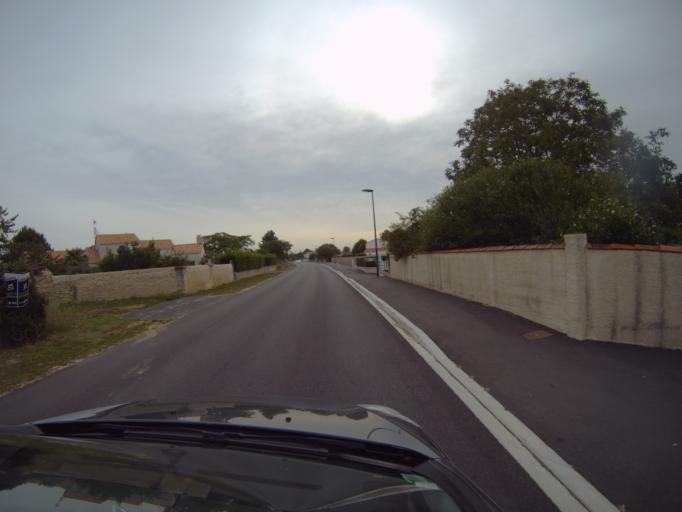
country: FR
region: Pays de la Loire
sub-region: Departement de la Vendee
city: Angles
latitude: 46.4060
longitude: -1.3887
